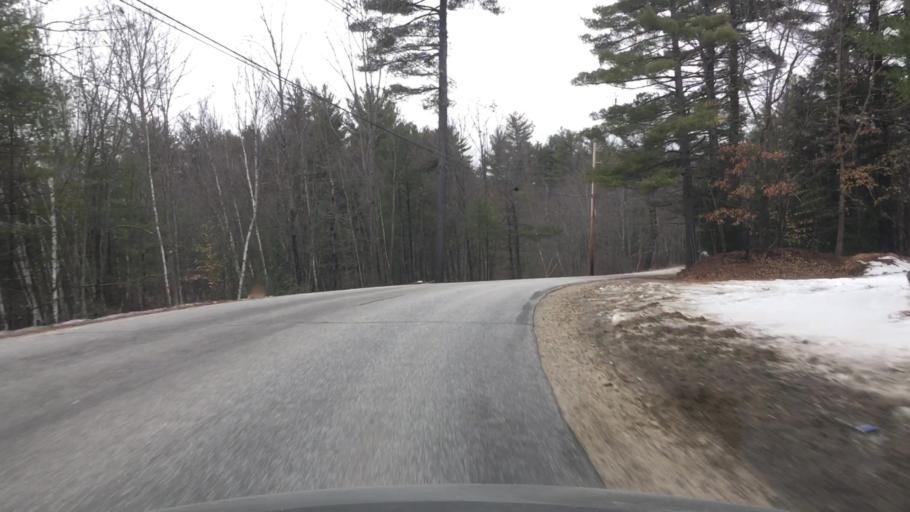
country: US
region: New Hampshire
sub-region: Hillsborough County
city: Goffstown
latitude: 42.9629
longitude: -71.6216
